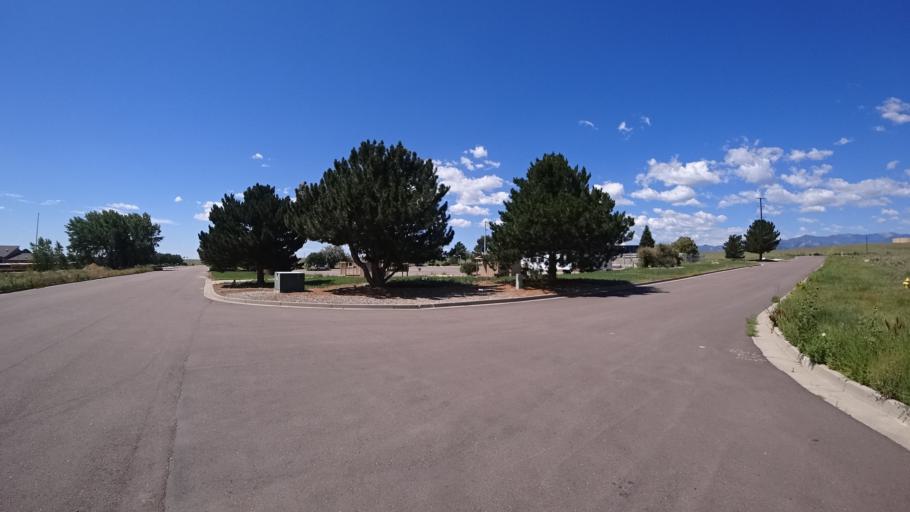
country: US
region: Colorado
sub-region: El Paso County
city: Security-Widefield
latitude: 38.7674
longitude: -104.6701
